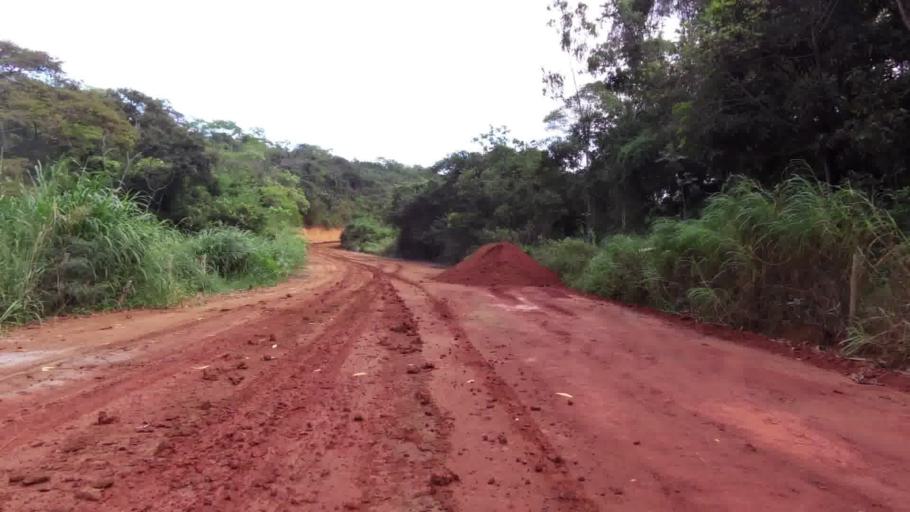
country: BR
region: Espirito Santo
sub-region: Piuma
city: Piuma
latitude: -20.8133
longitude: -40.6724
